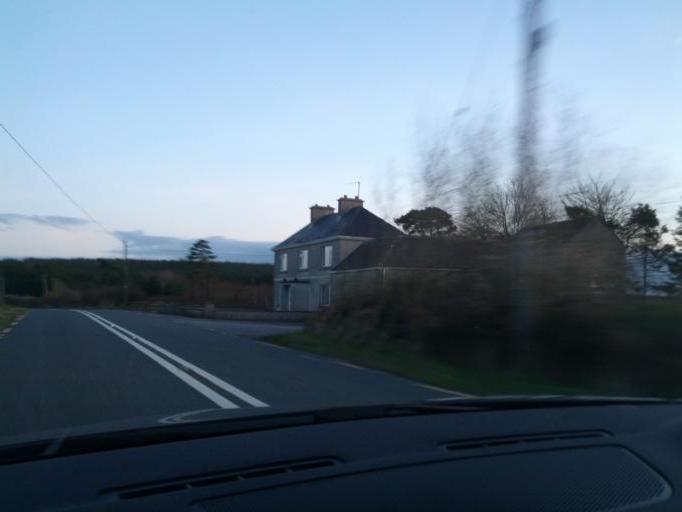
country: IE
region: Connaught
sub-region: Roscommon
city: Boyle
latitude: 53.9139
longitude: -8.2712
